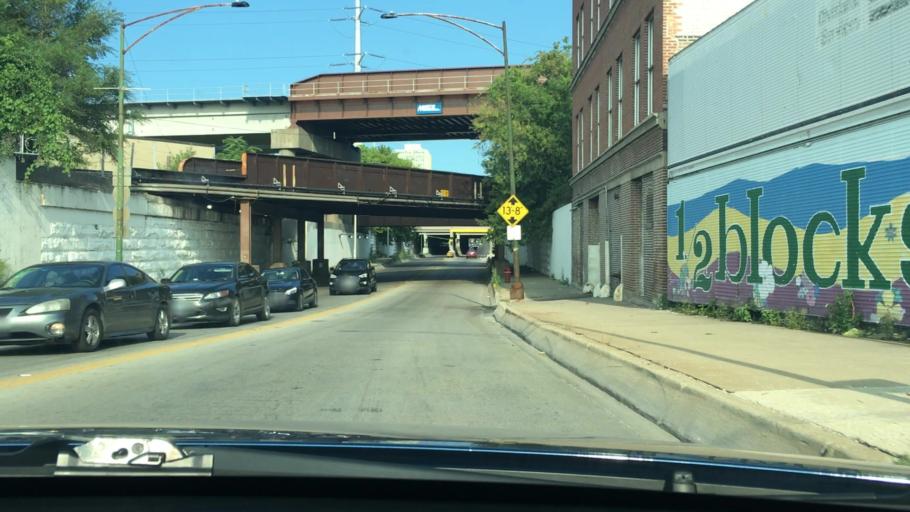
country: US
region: Illinois
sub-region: Cook County
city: Chicago
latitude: 41.7800
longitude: -87.6293
